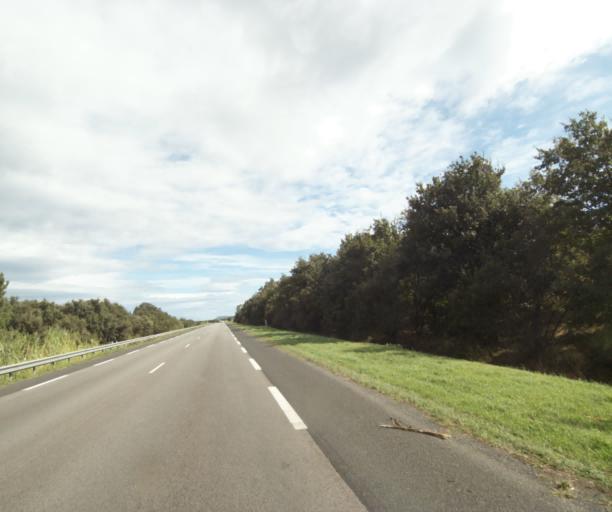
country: FR
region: Languedoc-Roussillon
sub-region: Departement des Pyrenees-Orientales
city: Sant Andreu de Sureda
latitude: 42.5556
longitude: 2.9843
